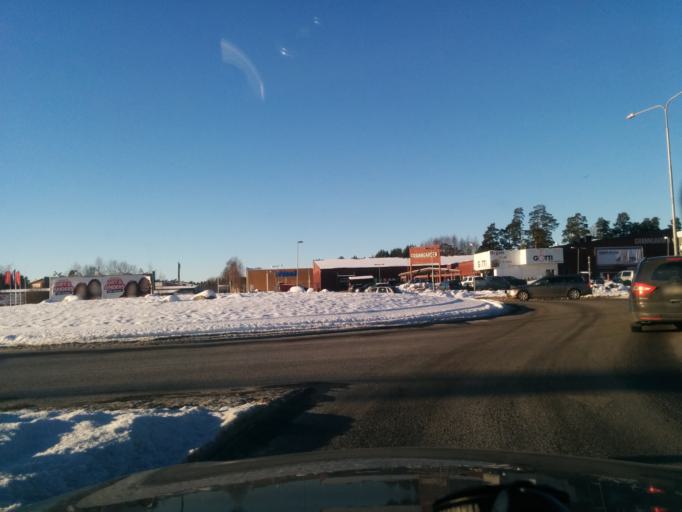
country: SE
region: Stockholm
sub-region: Taby Kommun
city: Taby
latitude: 59.4622
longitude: 18.1323
